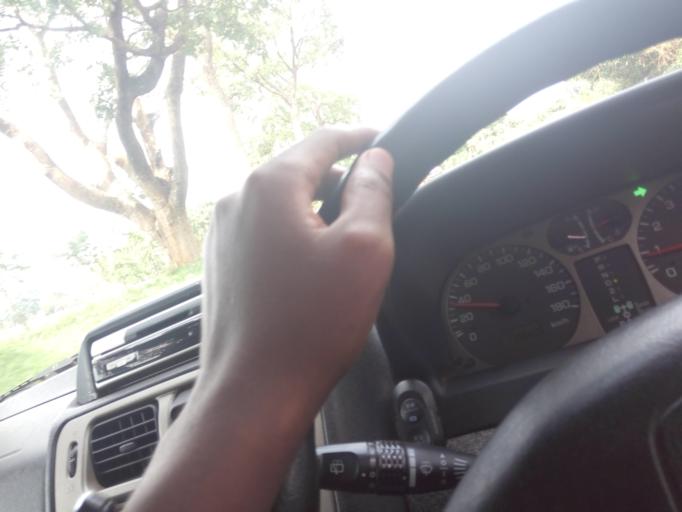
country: UG
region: Western Region
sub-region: Masindi District
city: Masindi
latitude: 1.6916
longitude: 31.7195
